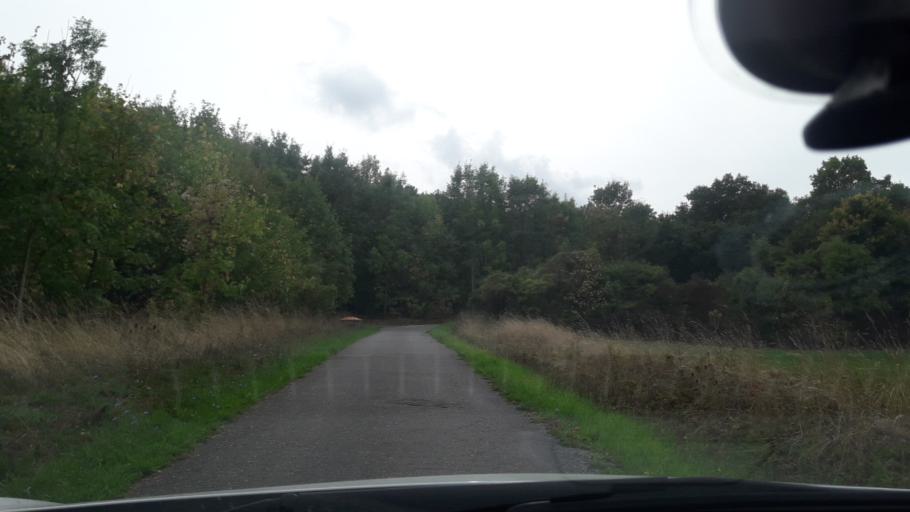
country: DE
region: Lower Saxony
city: Elbe
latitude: 52.0892
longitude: 10.3656
